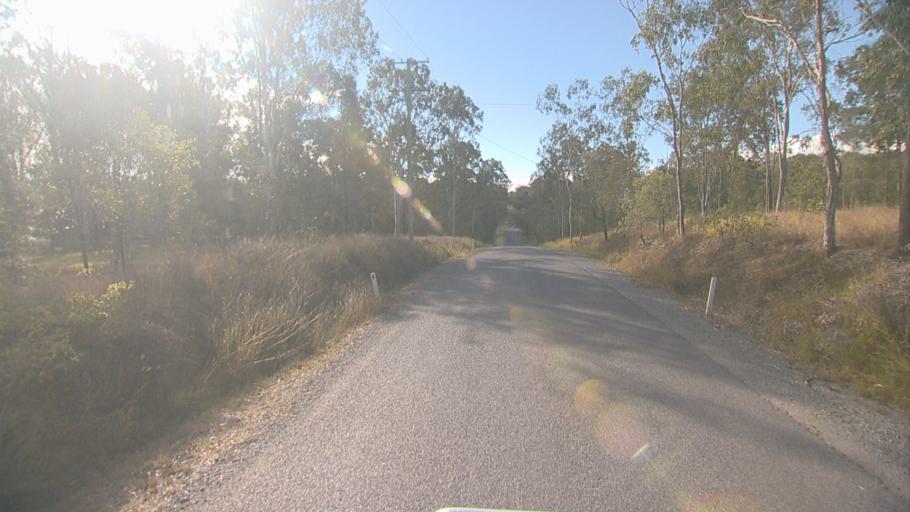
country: AU
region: Queensland
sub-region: Logan
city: Cedar Vale
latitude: -27.8273
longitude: 153.0623
